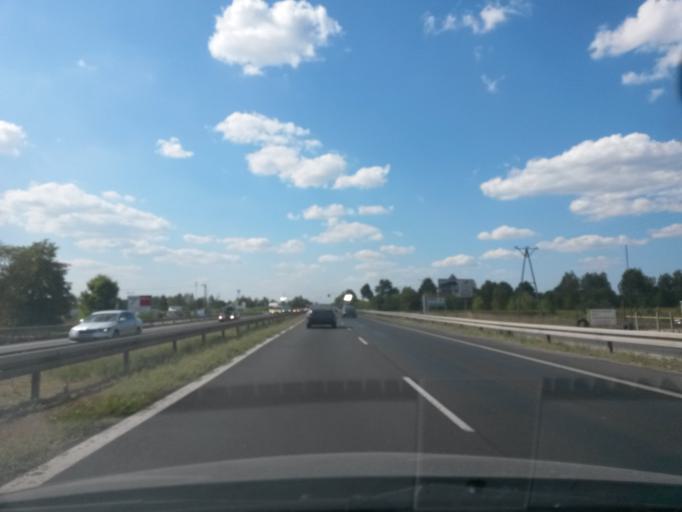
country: PL
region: Masovian Voivodeship
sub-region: Powiat warszawski zachodni
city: Dziekanow Lesny
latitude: 52.3539
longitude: 20.8468
